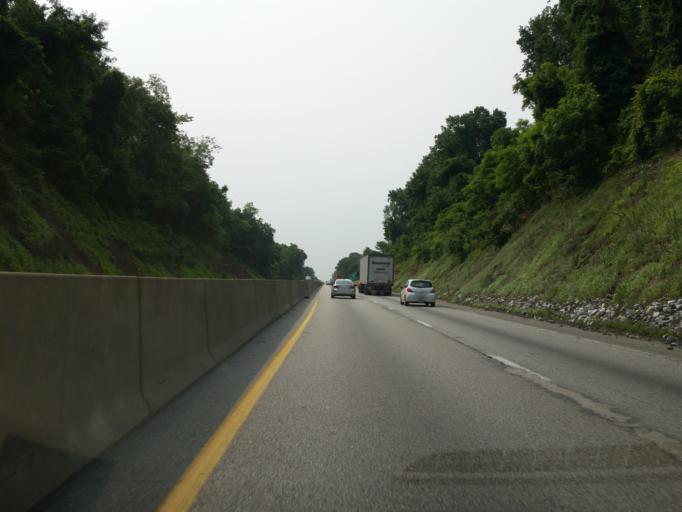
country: US
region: Pennsylvania
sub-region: York County
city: Valley Green
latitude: 40.1001
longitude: -76.7770
